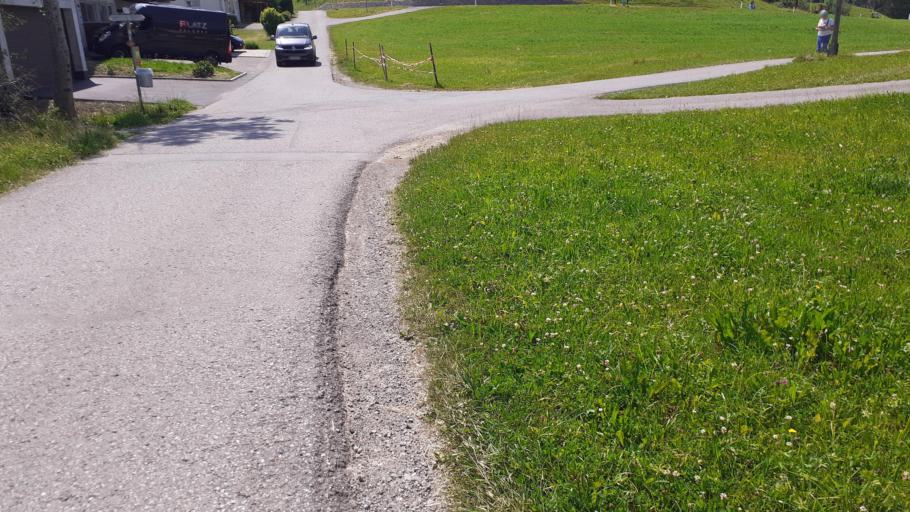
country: AT
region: Vorarlberg
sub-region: Politischer Bezirk Bregenz
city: Doren
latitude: 47.4595
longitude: 9.8371
